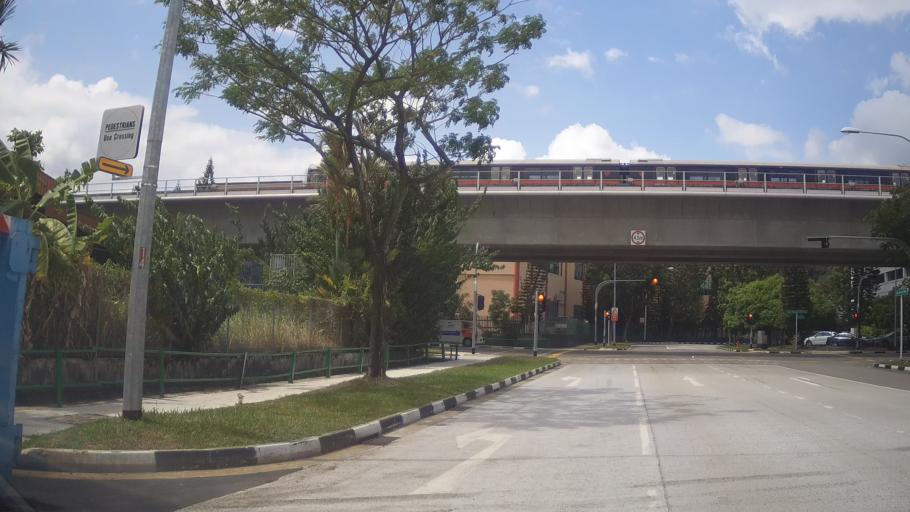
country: MY
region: Johor
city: Johor Bahru
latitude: 1.3267
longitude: 103.6697
